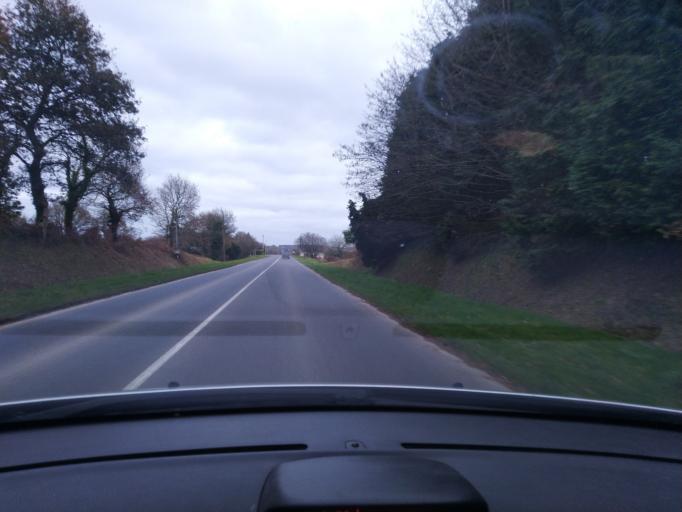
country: FR
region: Brittany
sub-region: Departement du Finistere
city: Guerlesquin
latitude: 48.5652
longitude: -3.5316
